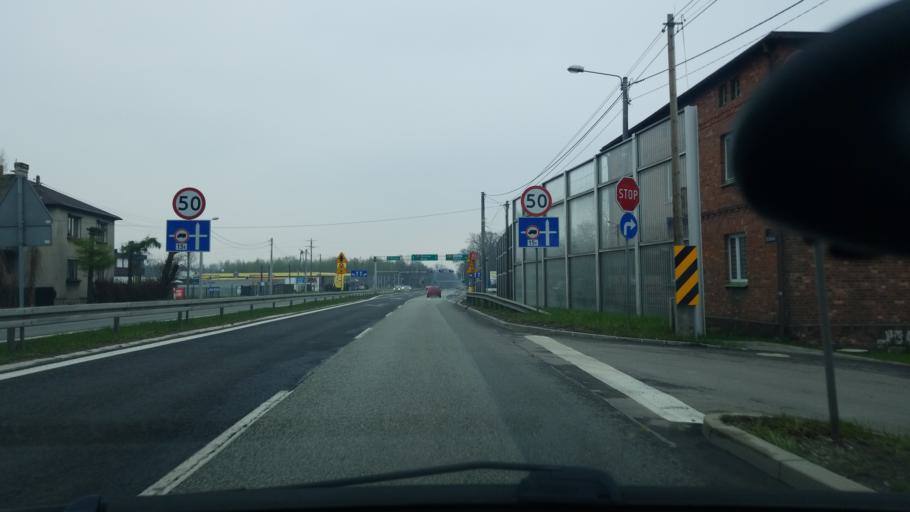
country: PL
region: Silesian Voivodeship
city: Gardawice
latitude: 50.1226
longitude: 18.8161
